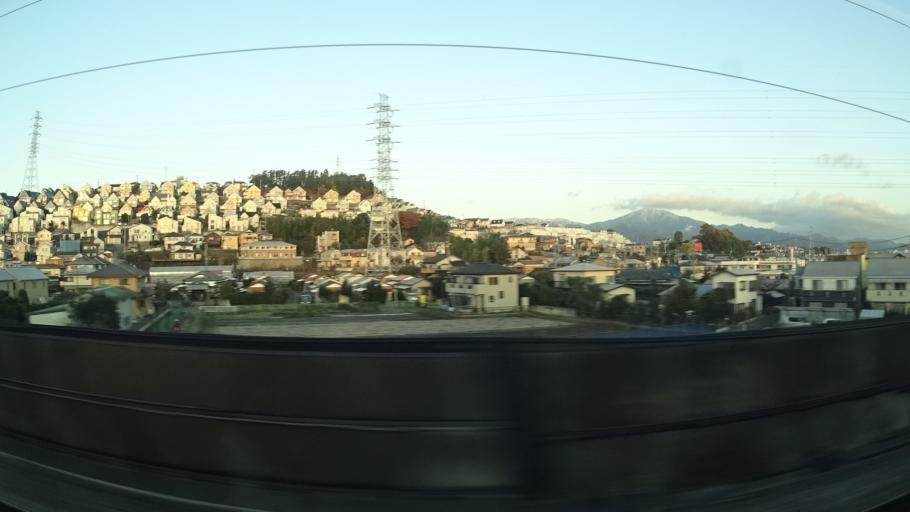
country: JP
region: Kanagawa
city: Oiso
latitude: 35.3401
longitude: 139.3055
